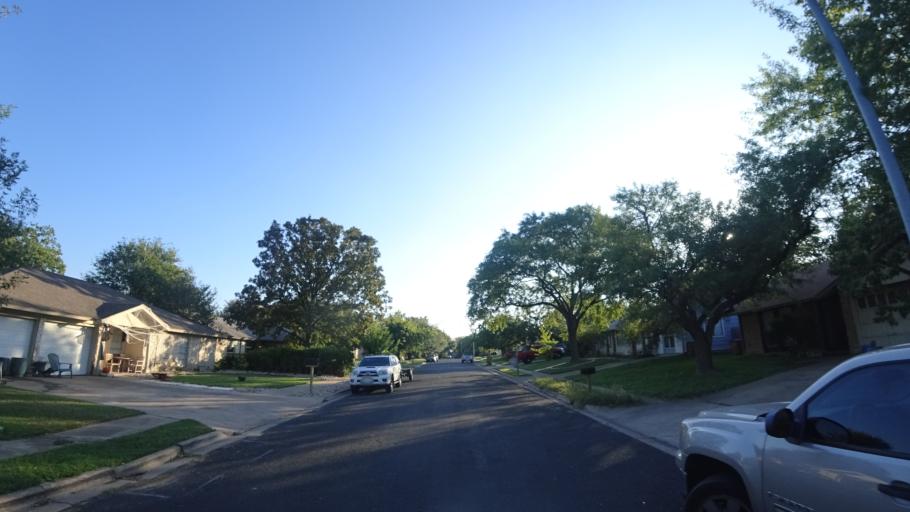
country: US
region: Texas
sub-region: Travis County
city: Wells Branch
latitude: 30.3619
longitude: -97.6764
